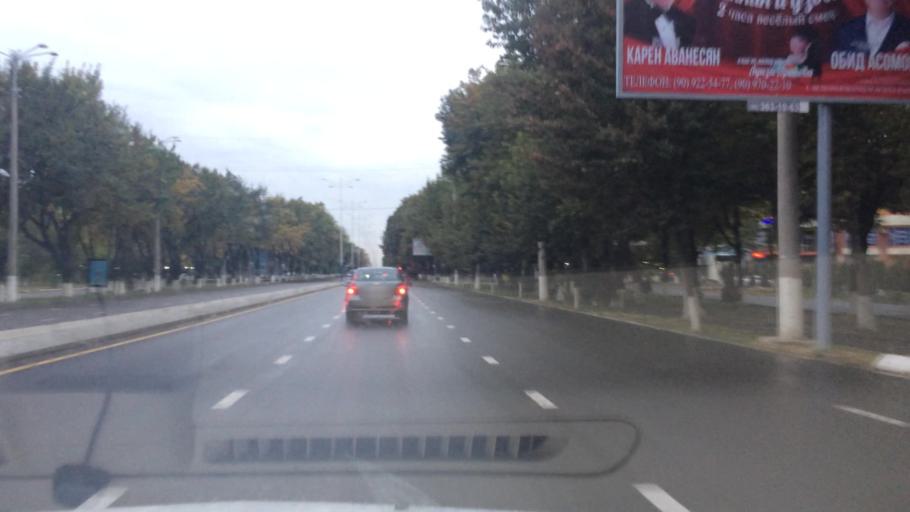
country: UZ
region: Toshkent Shahri
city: Tashkent
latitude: 41.2721
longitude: 69.2029
